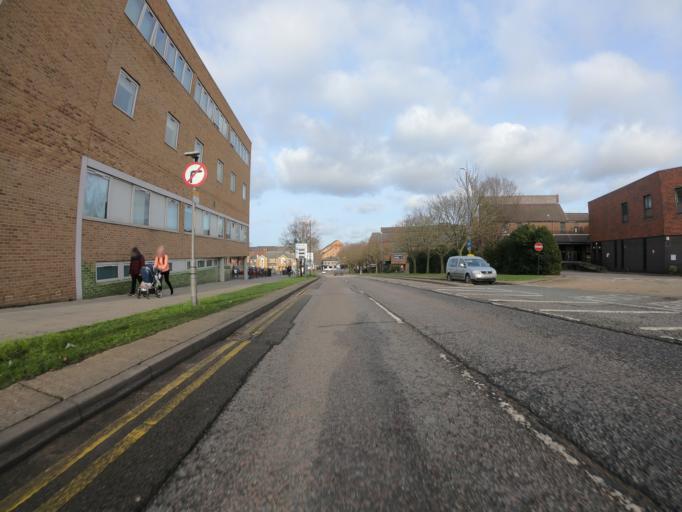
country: GB
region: England
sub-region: Kent
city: Gravesend
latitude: 51.4430
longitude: 0.3657
